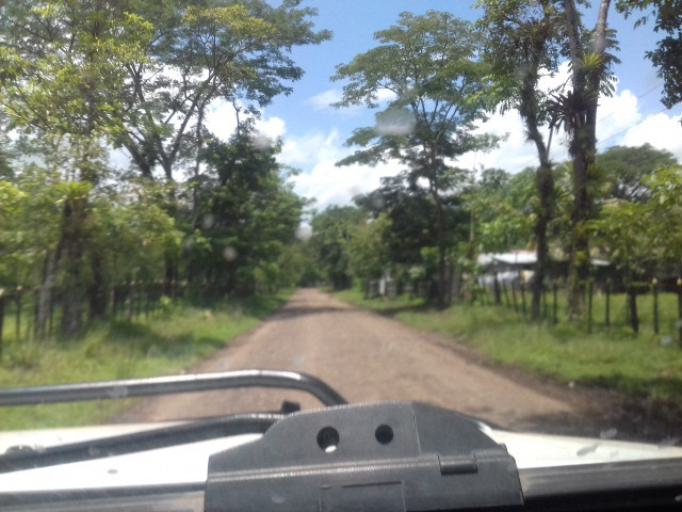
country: NI
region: Matagalpa
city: Rio Blanco
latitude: 12.9760
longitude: -85.3661
